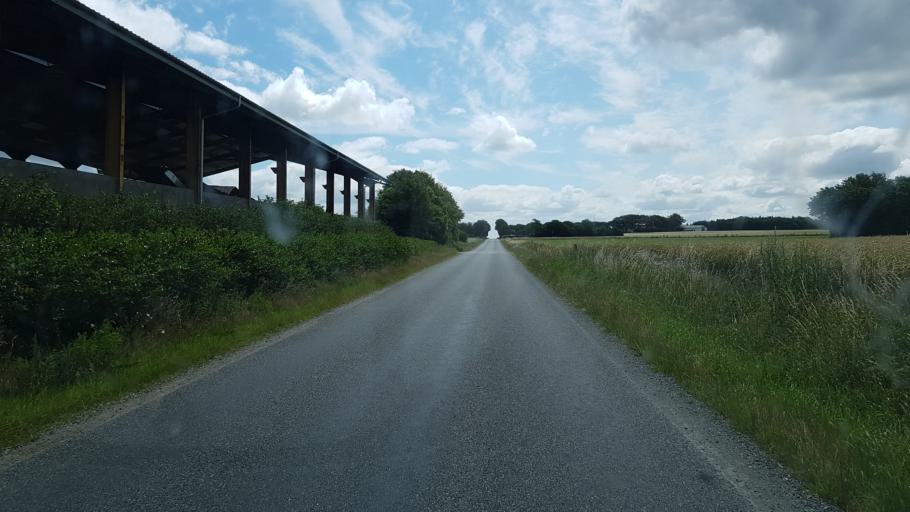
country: DK
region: South Denmark
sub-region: Vejen Kommune
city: Brorup
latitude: 55.4588
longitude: 8.9832
